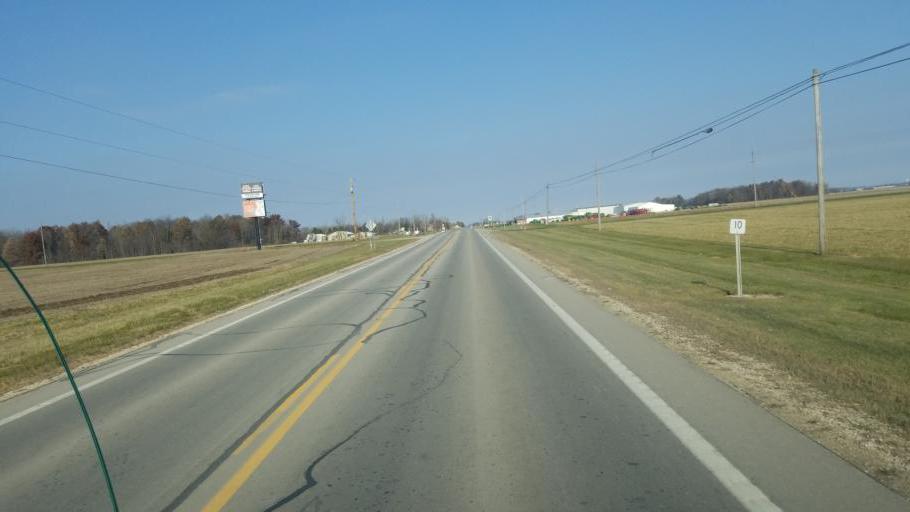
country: US
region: Ohio
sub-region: Mercer County
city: Coldwater
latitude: 40.4957
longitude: -84.6287
